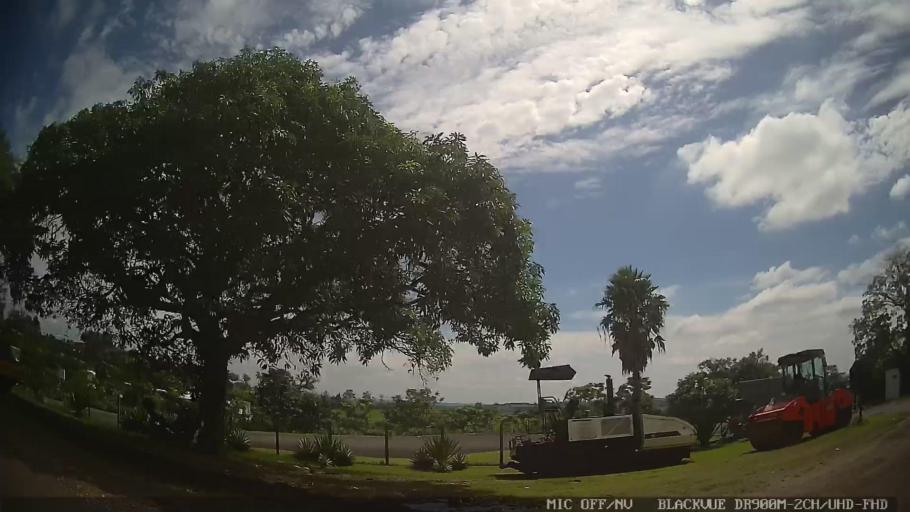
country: BR
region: Sao Paulo
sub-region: Laranjal Paulista
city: Laranjal Paulista
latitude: -23.0841
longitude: -47.7868
